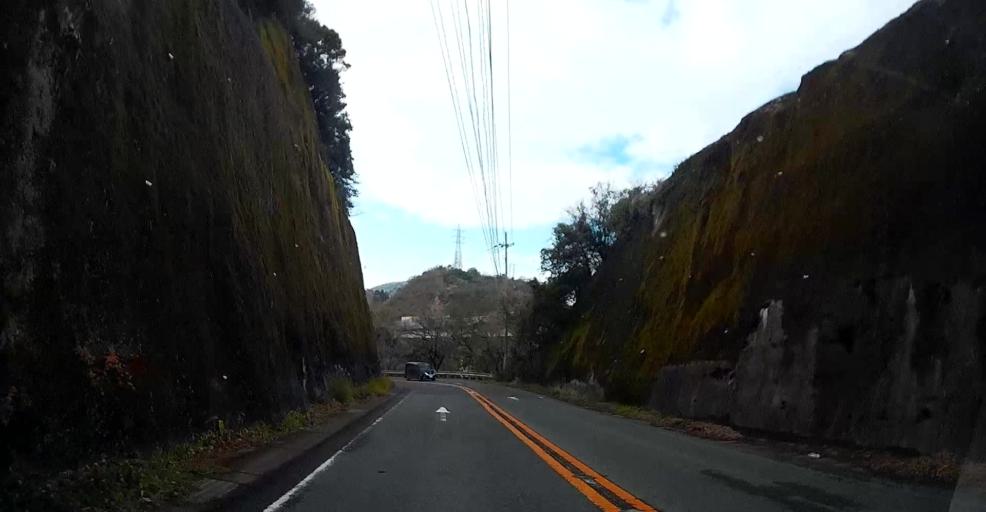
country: JP
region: Kumamoto
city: Yatsushiro
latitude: 32.6136
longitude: 130.4557
